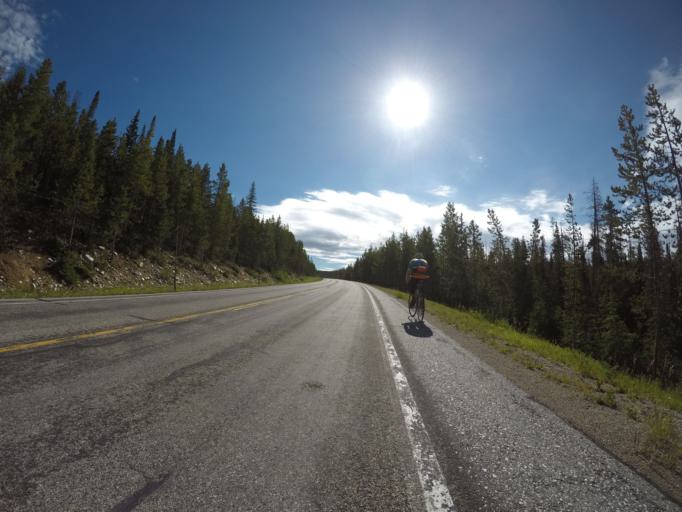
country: US
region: Wyoming
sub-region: Carbon County
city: Saratoga
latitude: 41.3229
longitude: -106.4557
